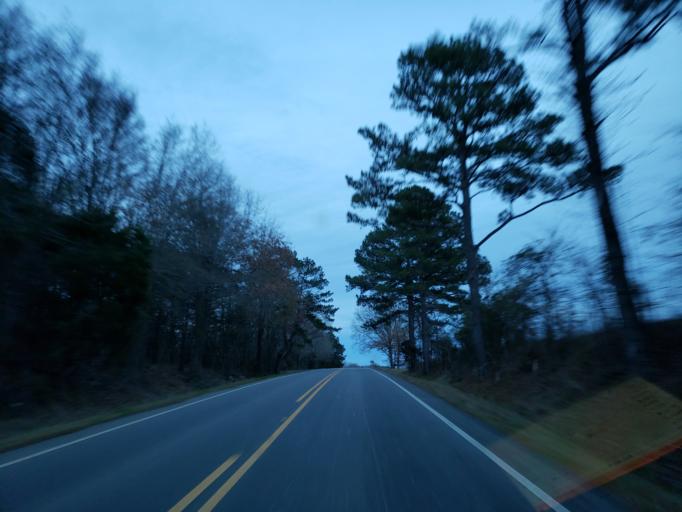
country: US
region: Alabama
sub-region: Sumter County
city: Livingston
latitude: 32.8113
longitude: -88.2554
